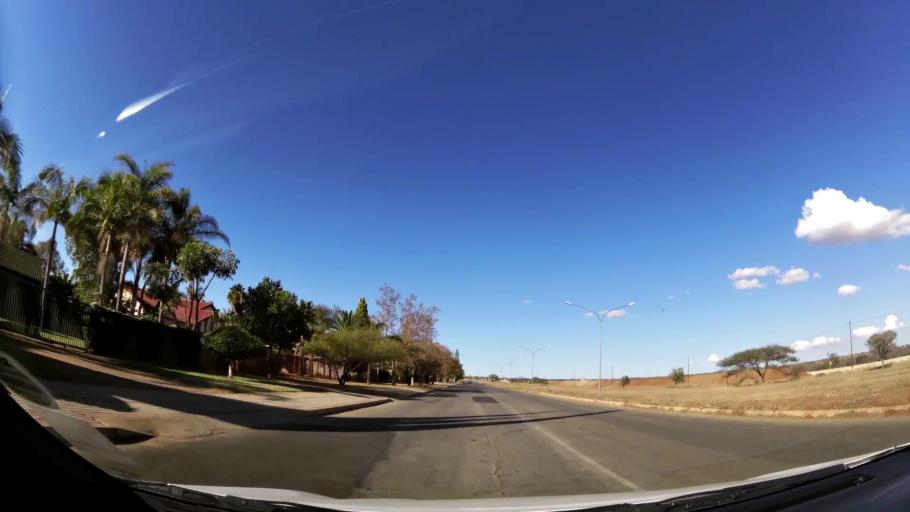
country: ZA
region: Limpopo
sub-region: Capricorn District Municipality
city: Polokwane
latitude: -23.9177
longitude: 29.4924
